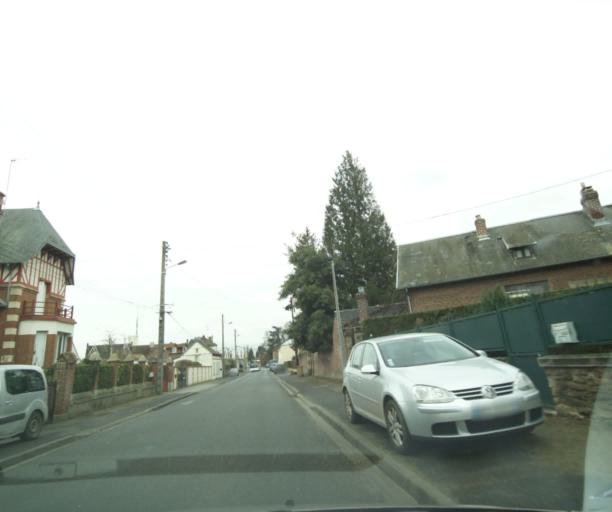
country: FR
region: Picardie
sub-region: Departement de l'Oise
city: Noyon
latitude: 49.5807
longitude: 3.0073
